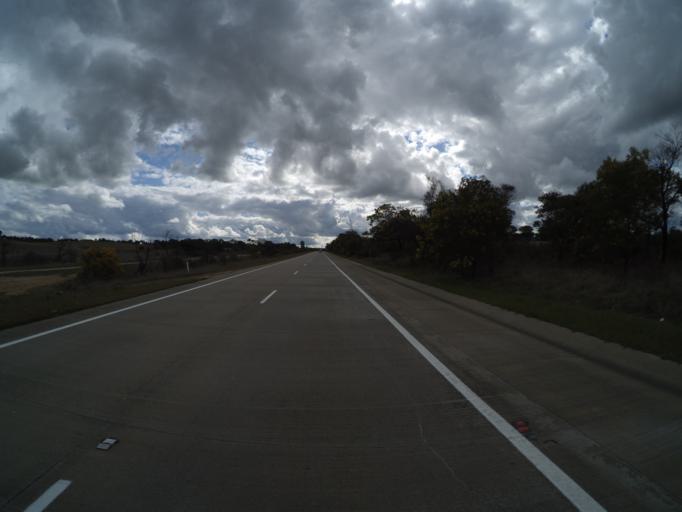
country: AU
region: New South Wales
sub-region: Yass Valley
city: Gundaroo
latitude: -34.7897
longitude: 149.2631
